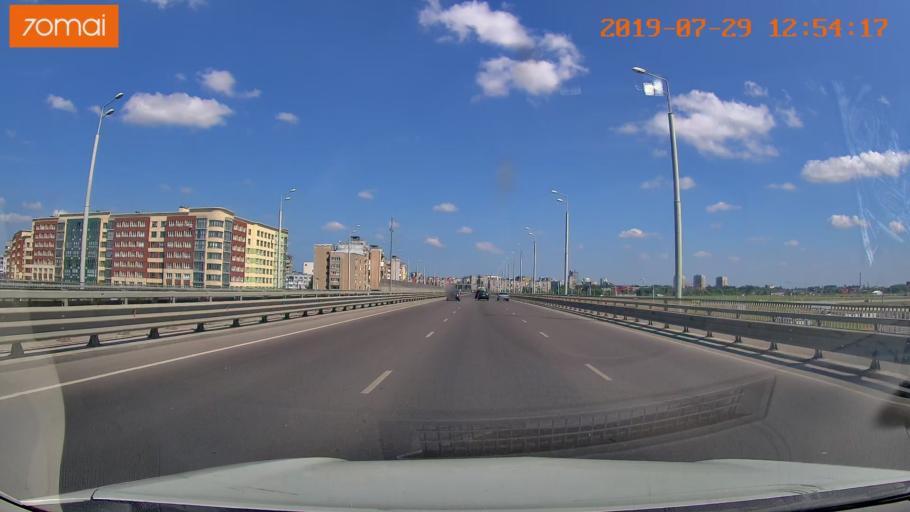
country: RU
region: Kaliningrad
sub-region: Gorod Kaliningrad
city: Kaliningrad
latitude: 54.6984
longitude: 20.5201
